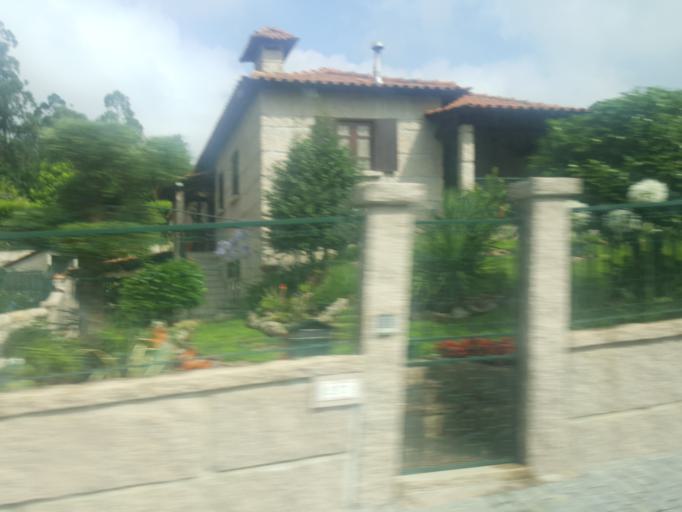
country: PT
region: Porto
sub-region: Penafiel
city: Perafita
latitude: 41.1625
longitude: -8.2031
